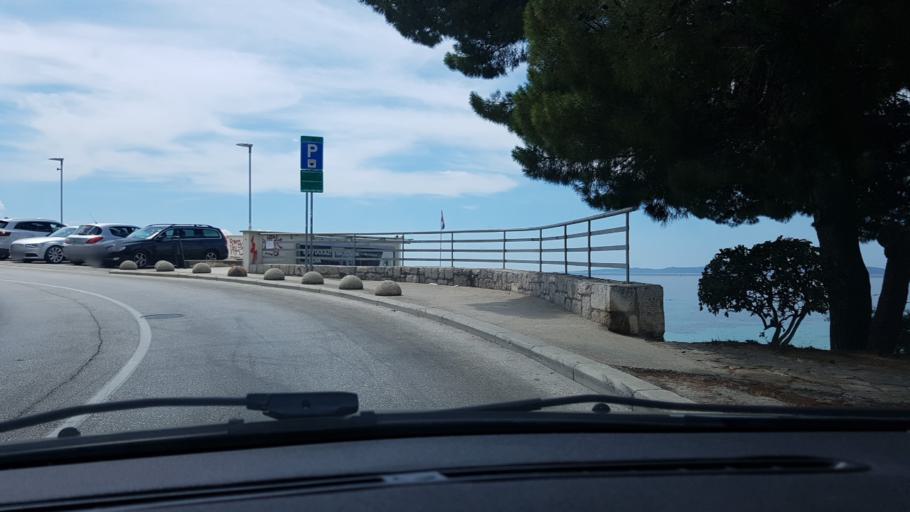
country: HR
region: Splitsko-Dalmatinska
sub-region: Grad Split
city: Split
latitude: 43.5025
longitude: 16.4484
